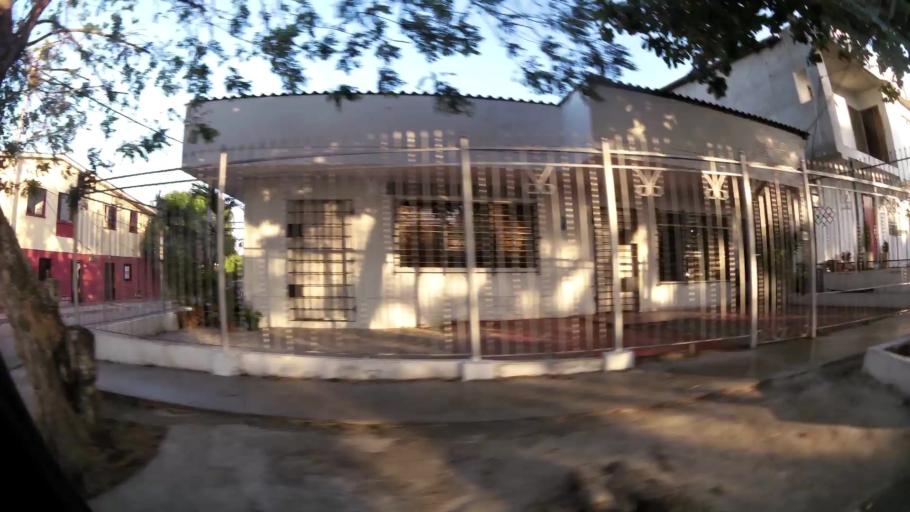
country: CO
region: Atlantico
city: Barranquilla
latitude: 10.9733
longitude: -74.8086
